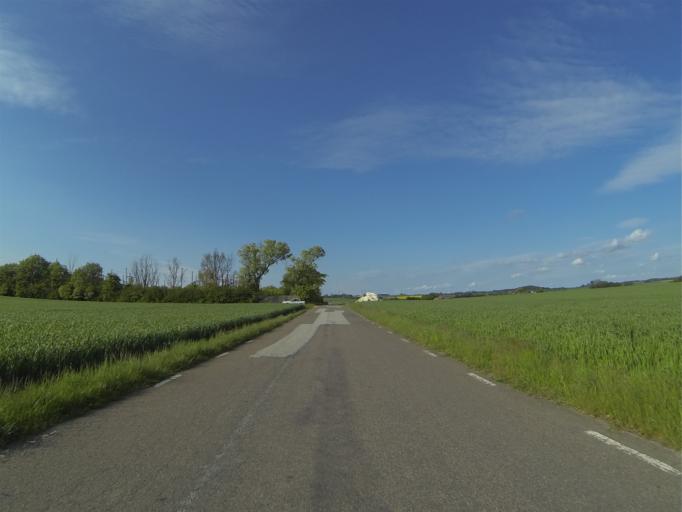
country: SE
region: Skane
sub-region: Staffanstorps Kommun
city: Staffanstorp
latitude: 55.6735
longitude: 13.2788
